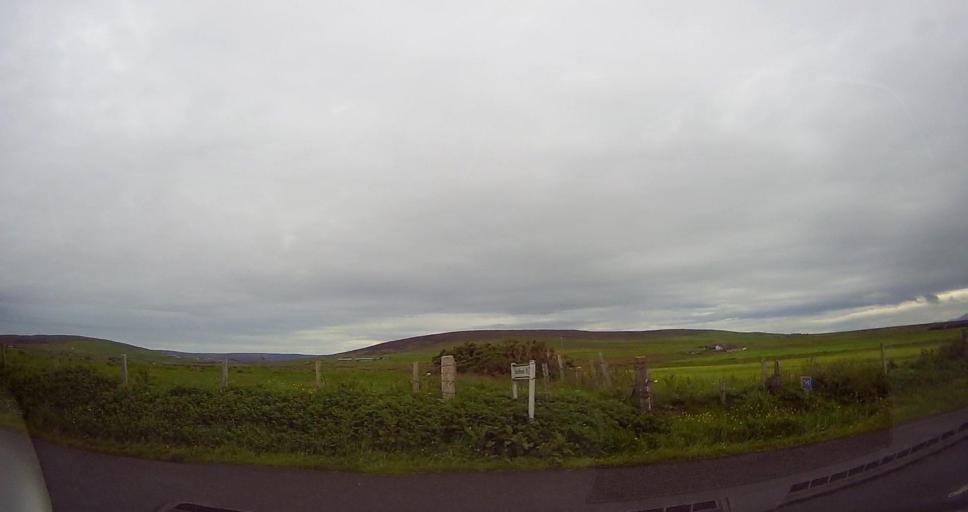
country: GB
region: Scotland
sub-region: Orkney Islands
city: Stromness
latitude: 59.1117
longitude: -3.2493
